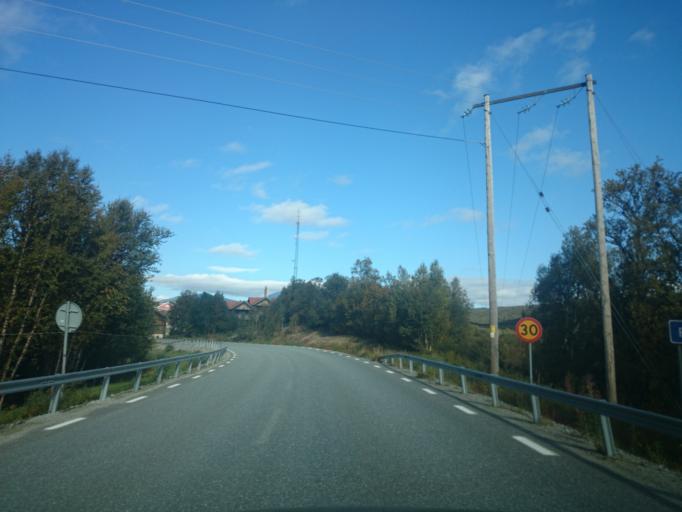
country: NO
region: Sor-Trondelag
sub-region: Tydal
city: Aas
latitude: 62.6996
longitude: 12.3940
